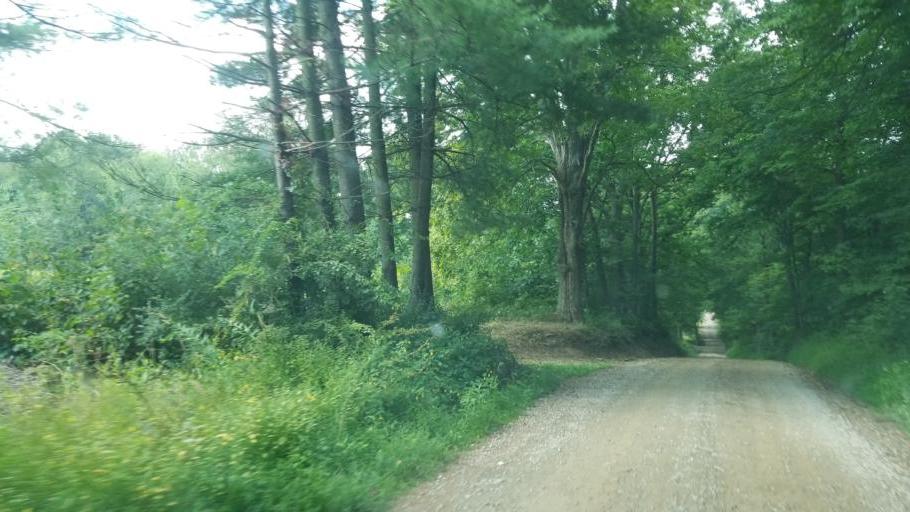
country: US
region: Ohio
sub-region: Knox County
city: Danville
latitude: 40.4610
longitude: -82.3076
